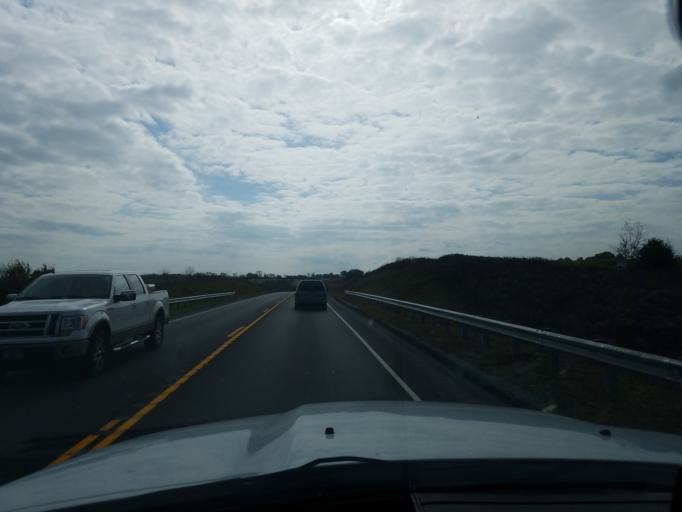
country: US
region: Kentucky
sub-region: Bullitt County
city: Mount Washington
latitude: 37.9479
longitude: -85.4670
